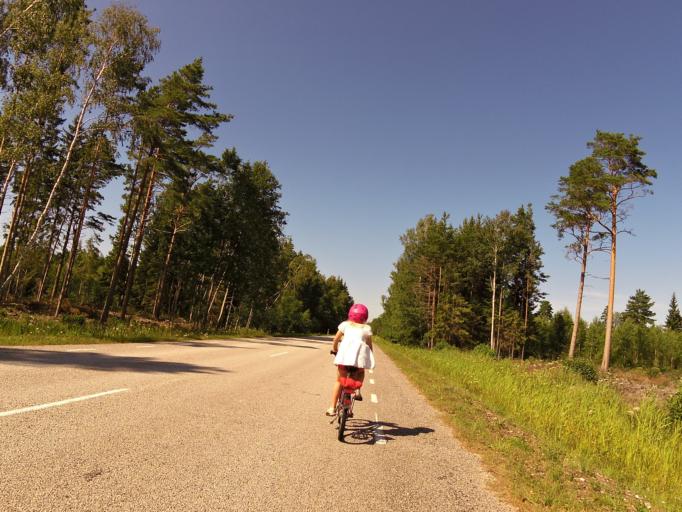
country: EE
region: Hiiumaa
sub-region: Kaerdla linn
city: Kardla
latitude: 58.8294
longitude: 22.4693
